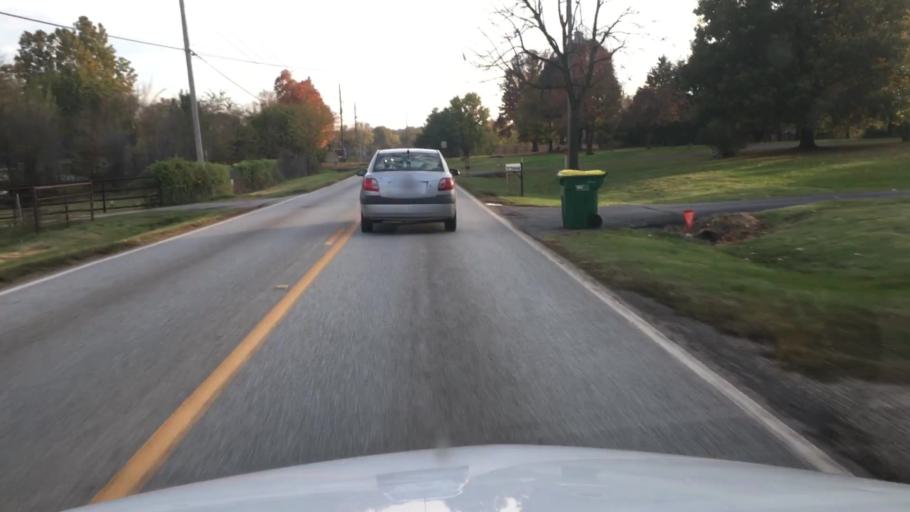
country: US
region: Arkansas
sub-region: Washington County
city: Elm Springs
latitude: 36.2142
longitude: -94.2317
